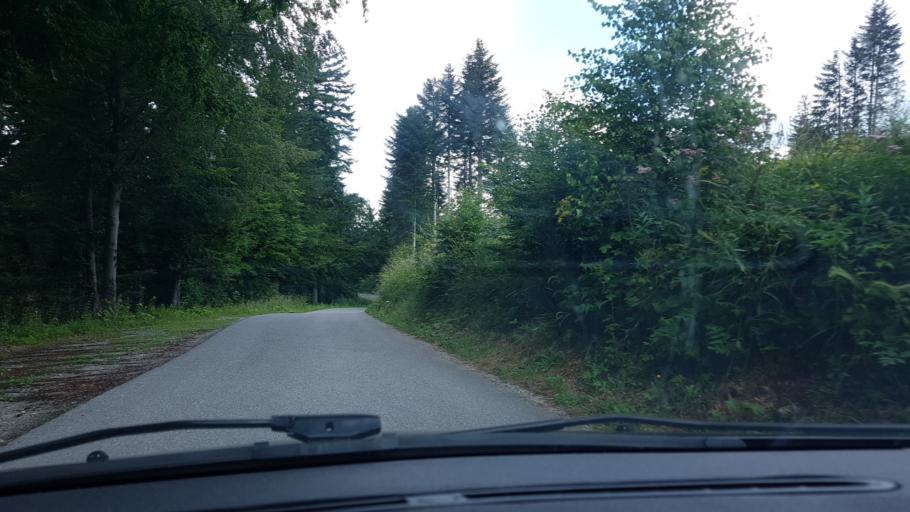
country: HR
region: Primorsko-Goranska
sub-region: Grad Delnice
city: Delnice
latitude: 45.3831
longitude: 14.6928
